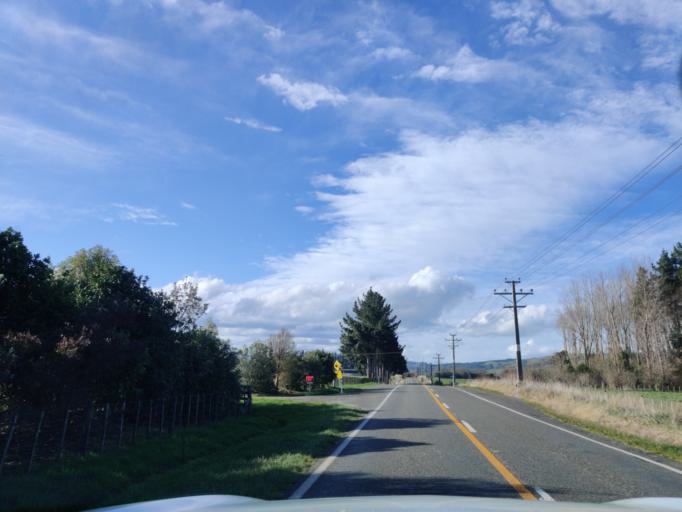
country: NZ
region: Manawatu-Wanganui
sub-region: Palmerston North City
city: Palmerston North
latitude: -40.3392
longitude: 175.7208
